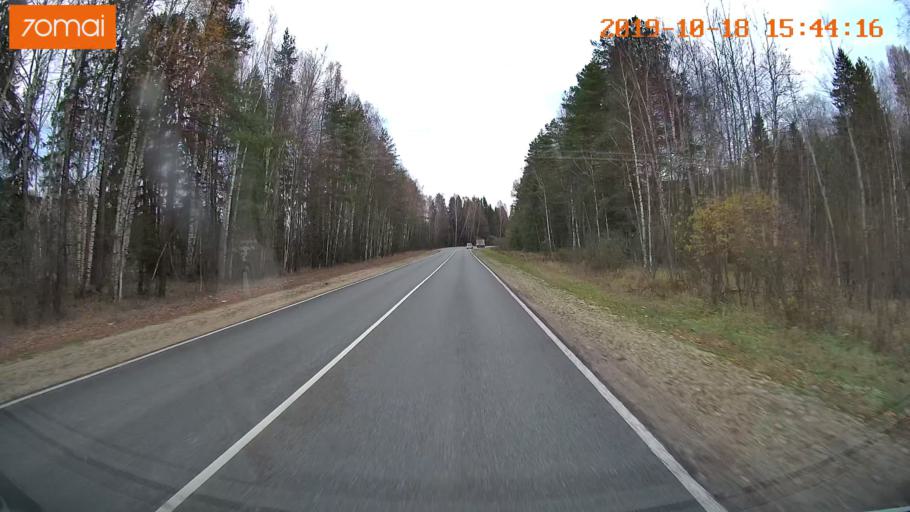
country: RU
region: Vladimir
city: Golovino
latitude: 55.9793
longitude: 40.5479
